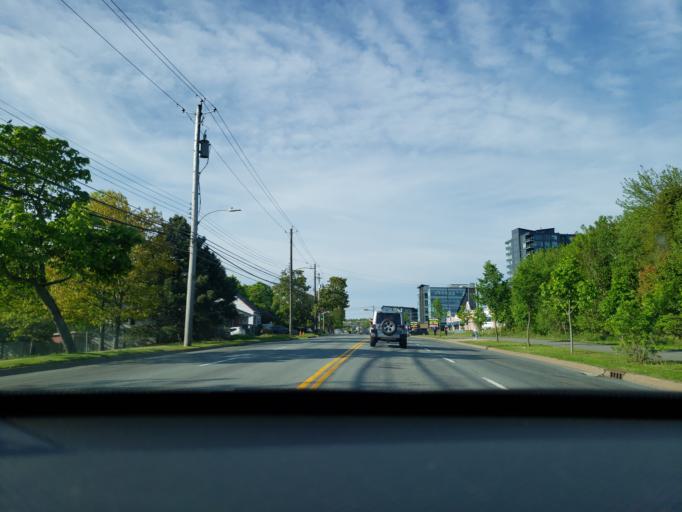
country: CA
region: Nova Scotia
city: Dartmouth
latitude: 44.6574
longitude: -63.6294
